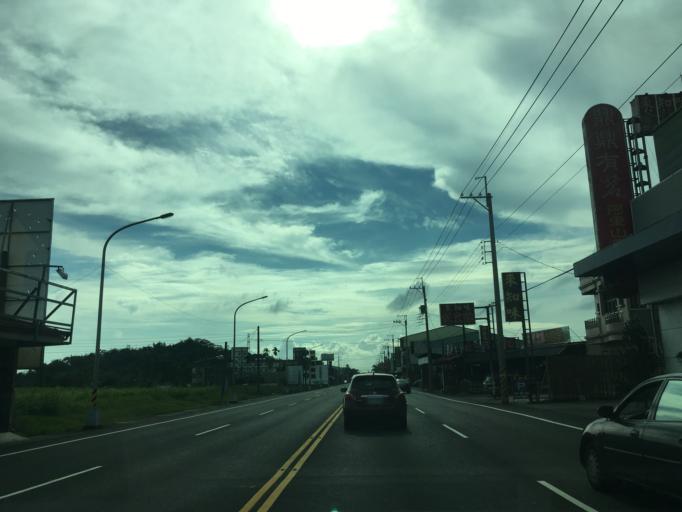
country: TW
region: Taiwan
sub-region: Chiayi
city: Jiayi Shi
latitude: 23.4433
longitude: 120.5100
